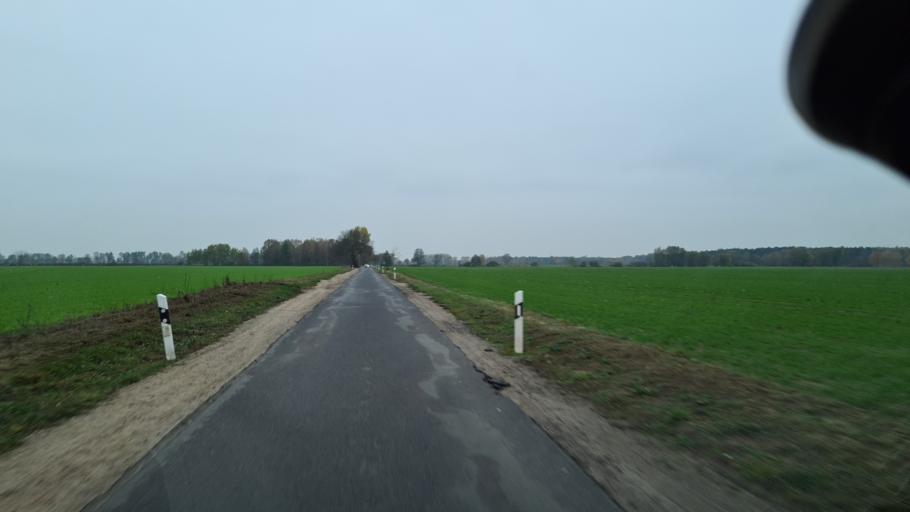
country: DE
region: Brandenburg
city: Lindow
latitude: 52.9308
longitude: 13.0108
